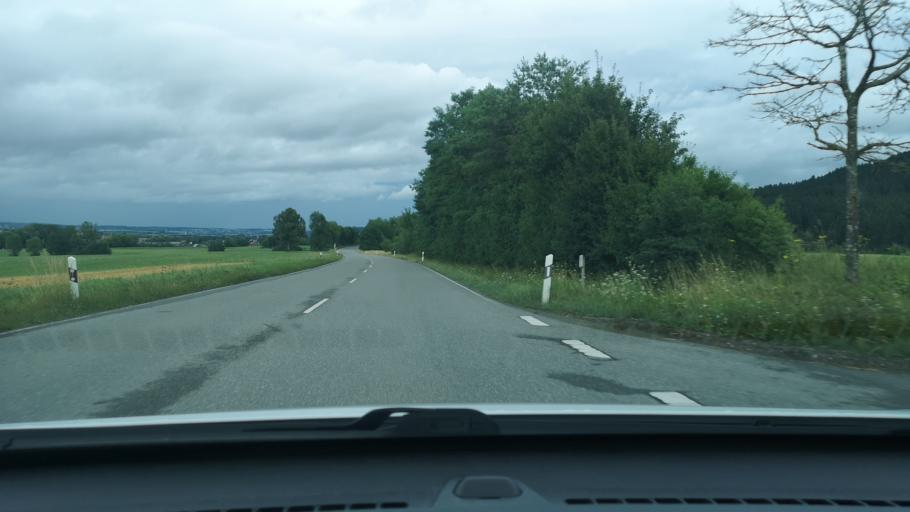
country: DE
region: Baden-Wuerttemberg
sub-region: Freiburg Region
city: Vohringen
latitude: 48.3056
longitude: 8.6309
